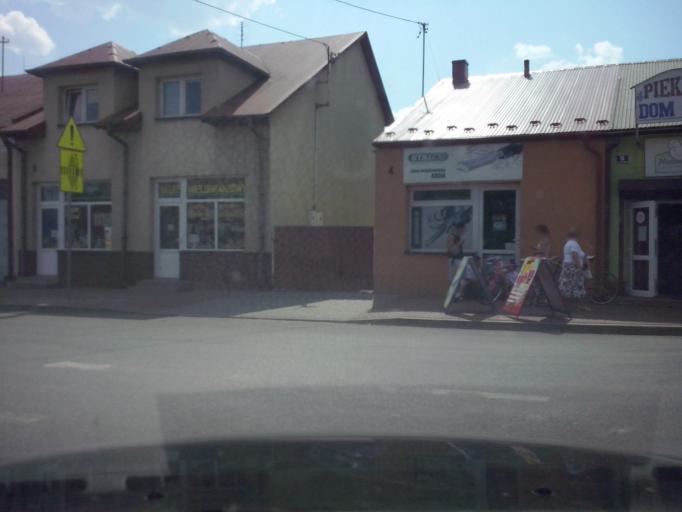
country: PL
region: Swietokrzyskie
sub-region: Powiat staszowski
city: Osiek
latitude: 50.5194
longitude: 21.4418
